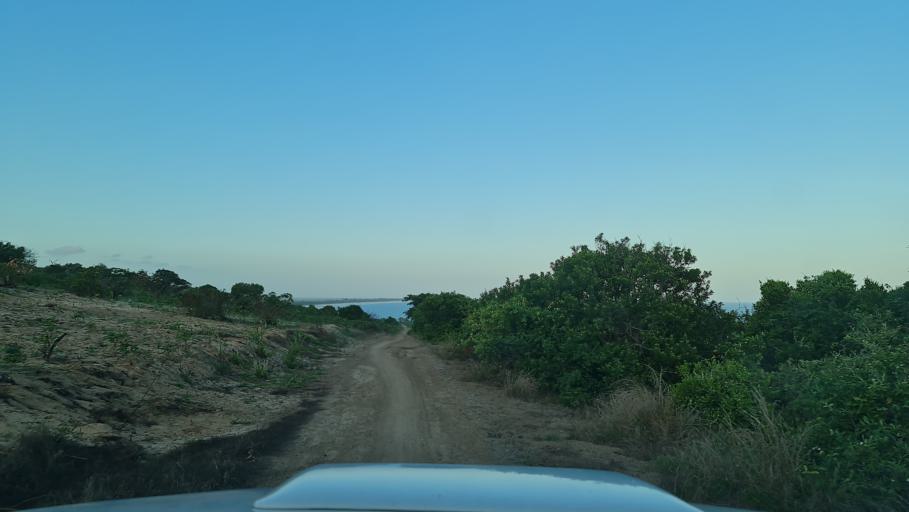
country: MZ
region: Nampula
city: Ilha de Mocambique
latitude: -15.6339
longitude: 40.4171
